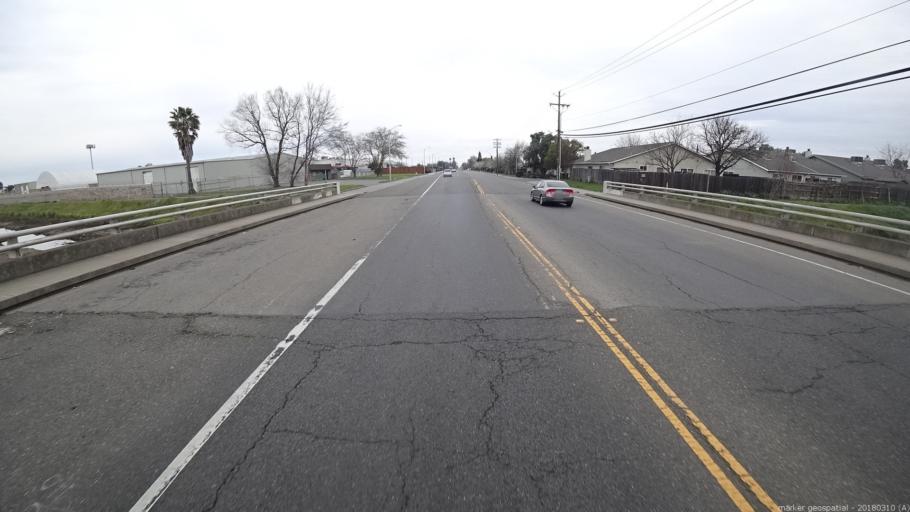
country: US
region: California
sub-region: Sacramento County
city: Florin
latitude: 38.4844
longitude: -121.3903
